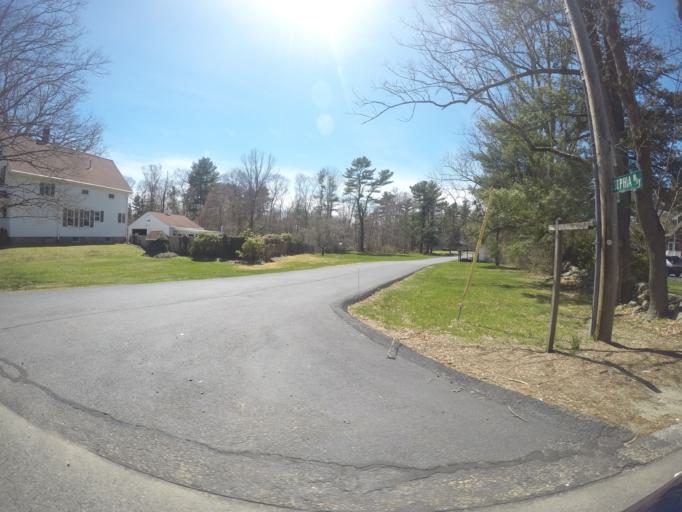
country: US
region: Massachusetts
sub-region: Bristol County
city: Easton
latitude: 42.0419
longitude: -71.0904
